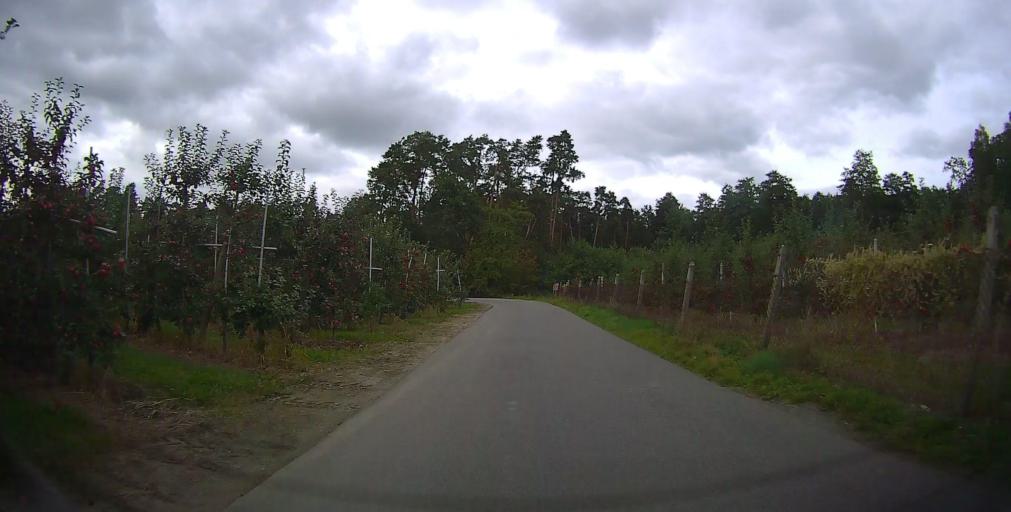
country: PL
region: Masovian Voivodeship
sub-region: Powiat grojecki
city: Goszczyn
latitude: 51.7743
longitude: 20.8640
